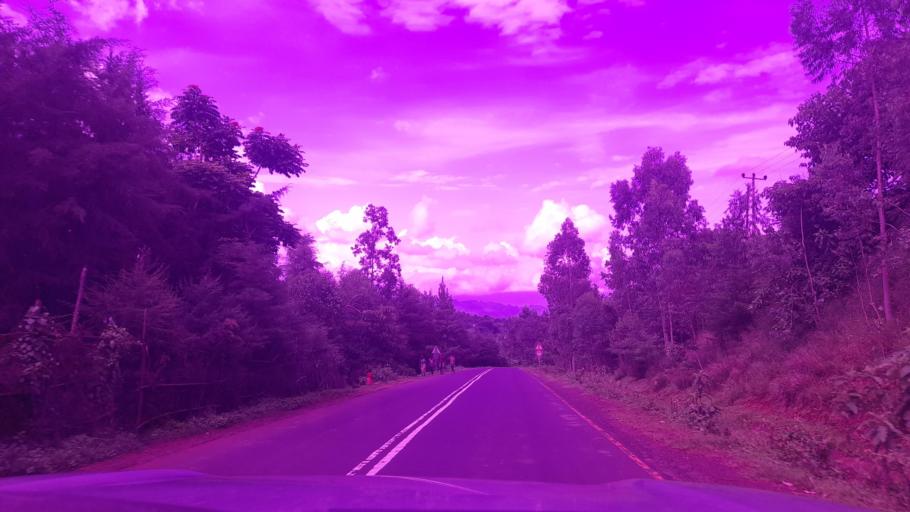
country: ET
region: Oromiya
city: Jima
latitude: 7.5177
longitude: 36.5293
